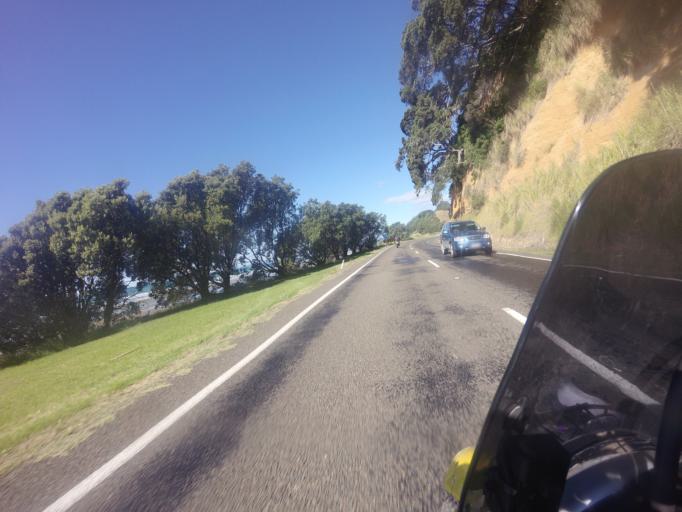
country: NZ
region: Bay of Plenty
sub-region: Opotiki District
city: Opotiki
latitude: -37.9913
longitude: 177.2144
